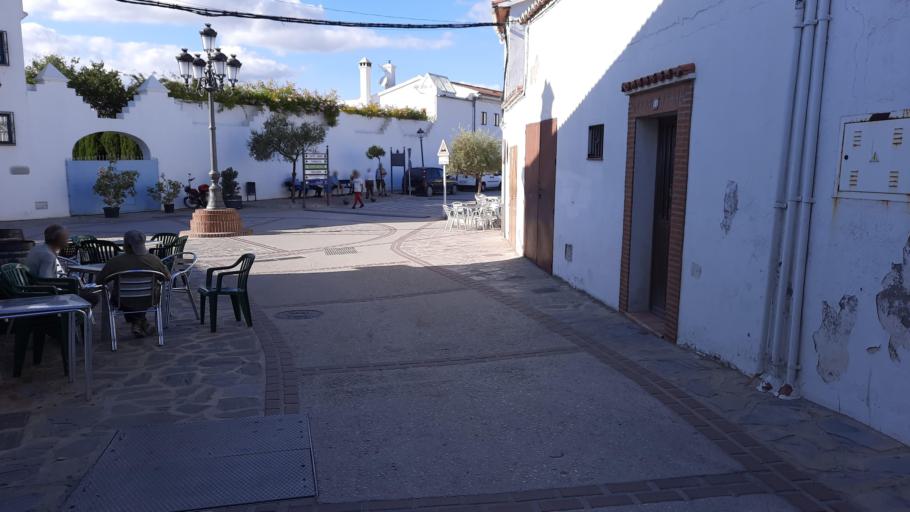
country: ES
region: Andalusia
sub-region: Provincia de Malaga
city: Gaucin
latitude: 36.5206
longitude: -5.3159
